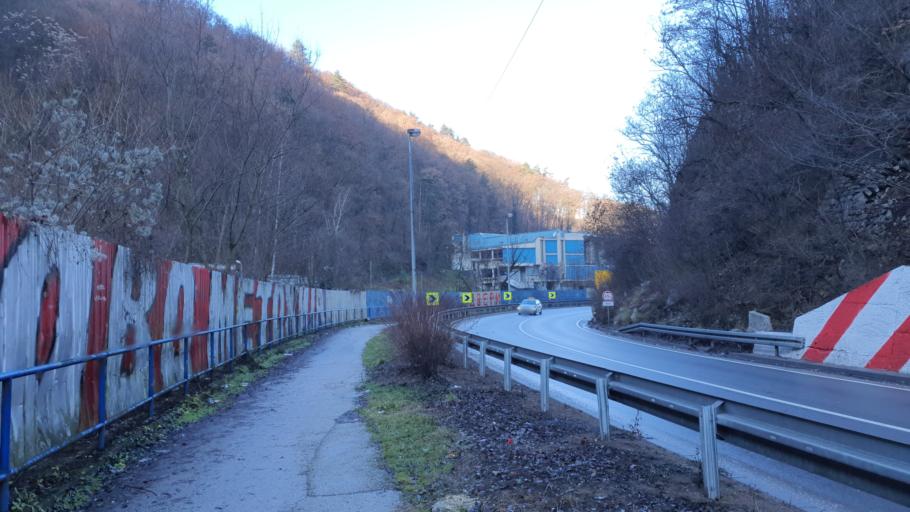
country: RS
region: Central Serbia
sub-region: Zlatiborski Okrug
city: Uzice
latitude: 43.8471
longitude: 19.8480
